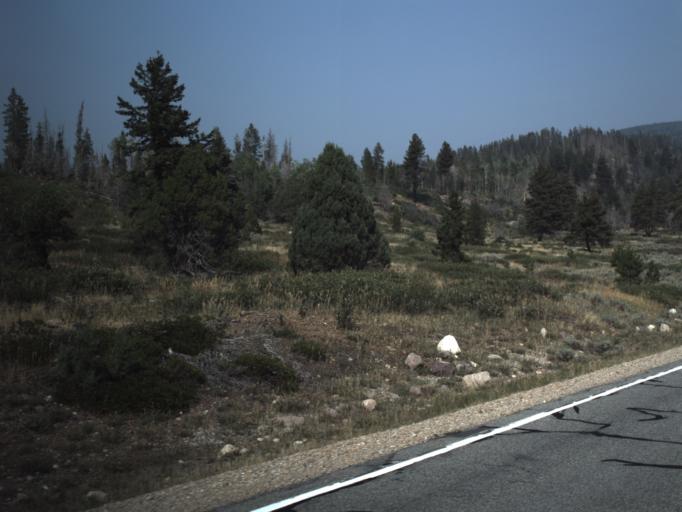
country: US
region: Utah
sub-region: Summit County
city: Francis
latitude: 40.5946
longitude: -111.0851
